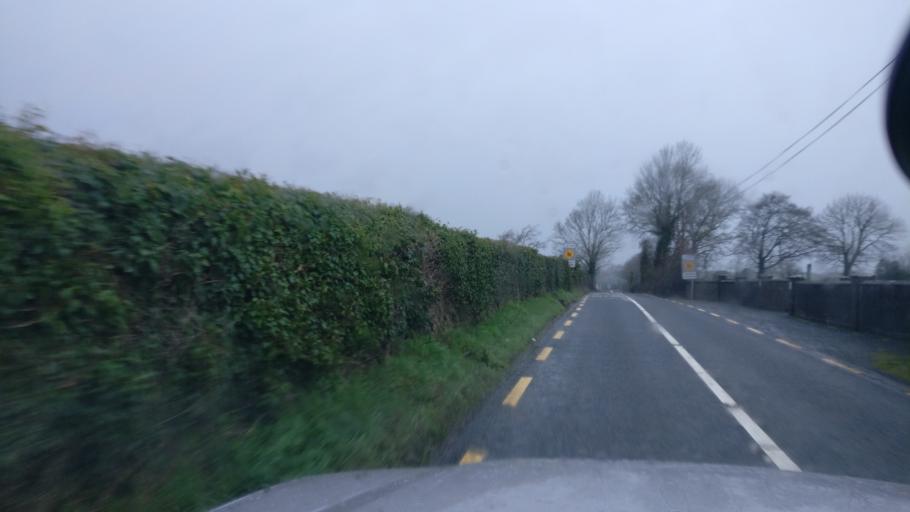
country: IE
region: Connaught
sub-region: County Galway
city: Loughrea
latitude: 53.1574
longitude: -8.4832
